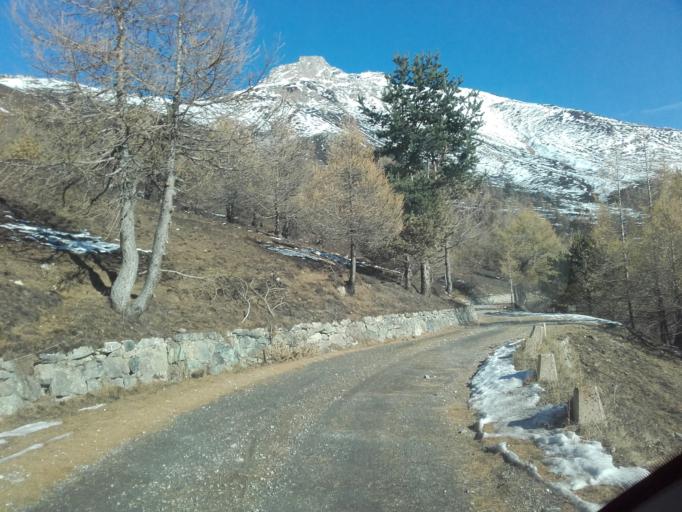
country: IT
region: Piedmont
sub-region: Provincia di Torino
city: Mompantero
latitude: 45.1743
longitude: 7.0628
